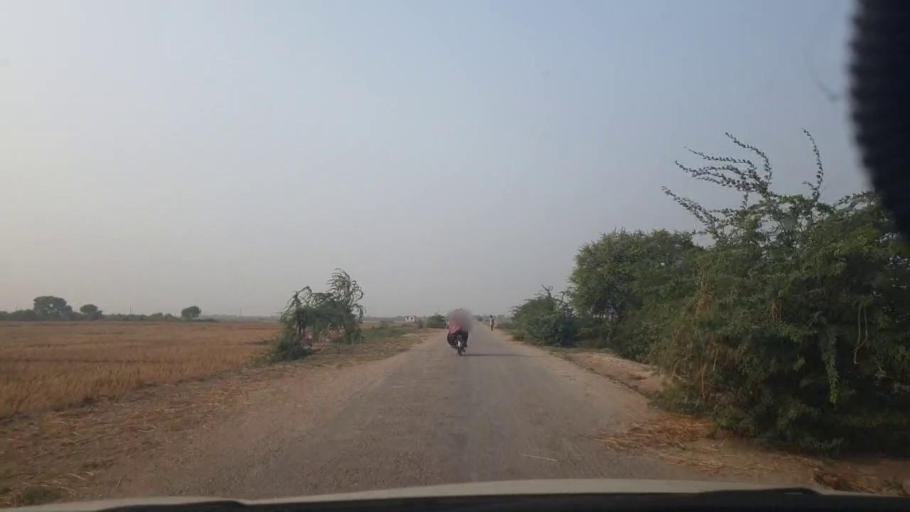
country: PK
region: Sindh
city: Bulri
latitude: 24.8136
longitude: 68.4074
